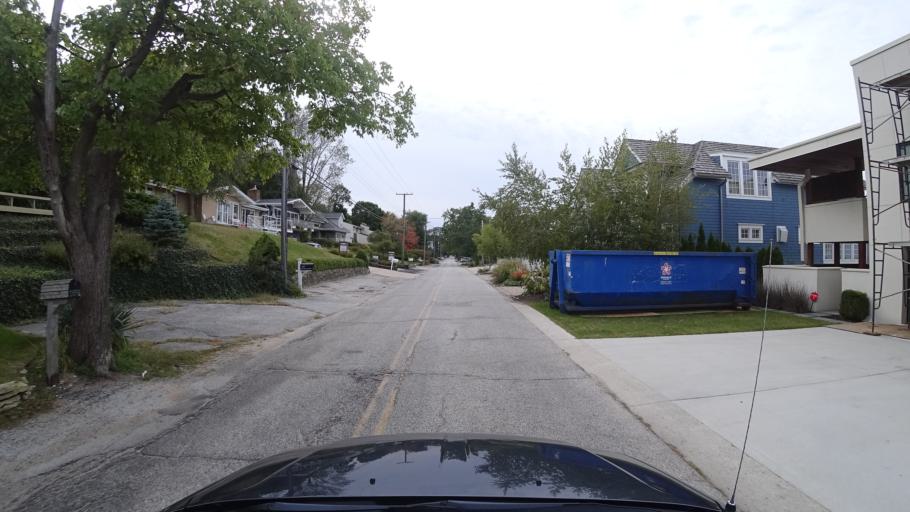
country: US
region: Indiana
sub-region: LaPorte County
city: Long Beach
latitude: 41.7440
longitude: -86.8601
